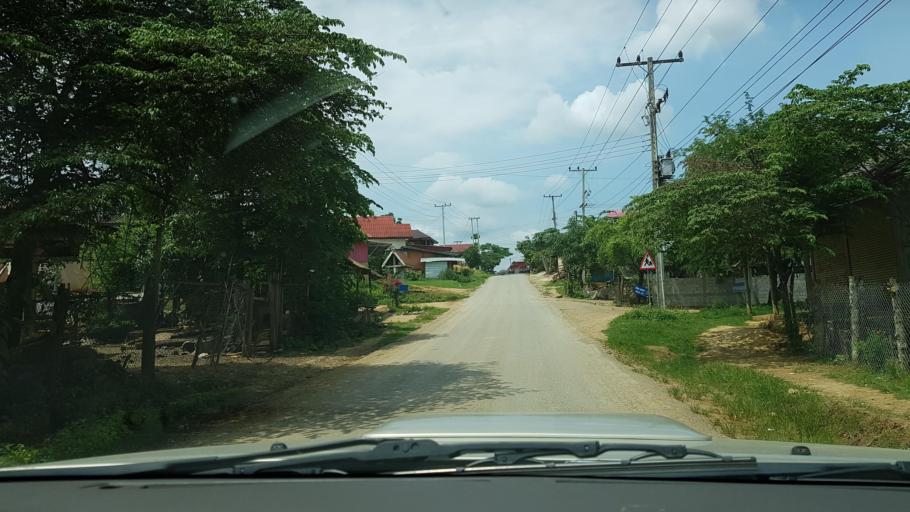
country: LA
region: Loungnamtha
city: Muang Nale
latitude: 20.0502
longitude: 101.3580
